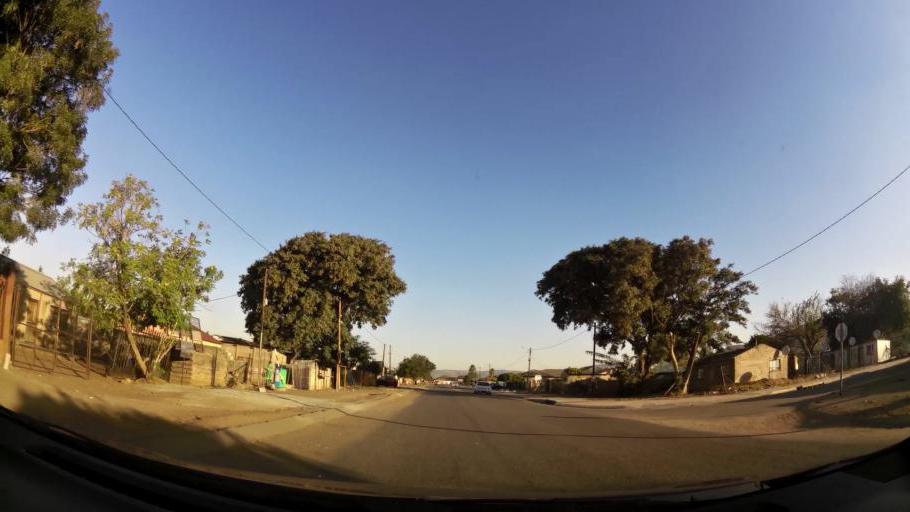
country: ZA
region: North-West
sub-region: Bojanala Platinum District Municipality
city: Rustenburg
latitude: -25.6292
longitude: 27.2155
